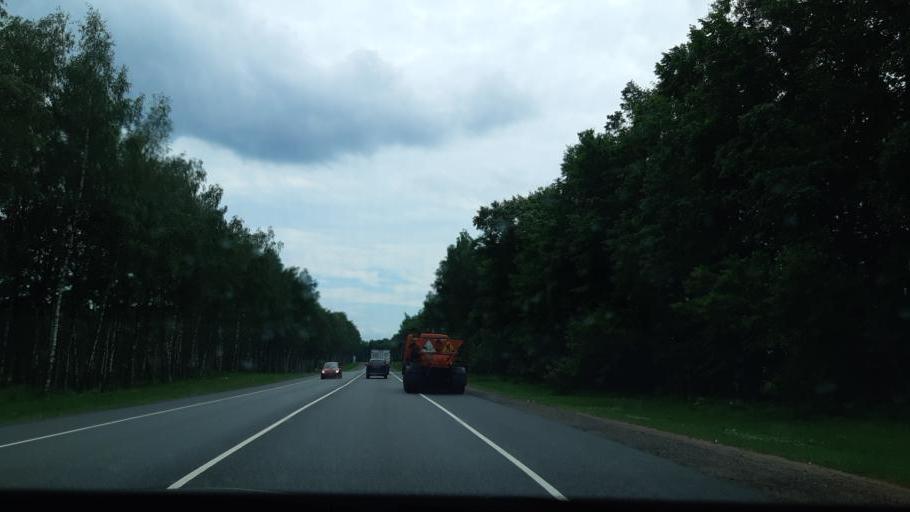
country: RU
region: Moskovskaya
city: Dorokhovo
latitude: 55.5007
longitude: 36.3470
